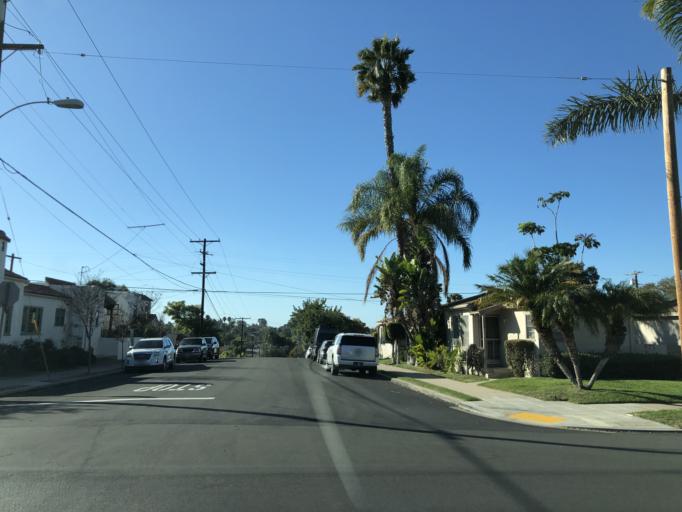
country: US
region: California
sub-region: San Diego County
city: San Diego
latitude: 32.7422
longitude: -117.1345
